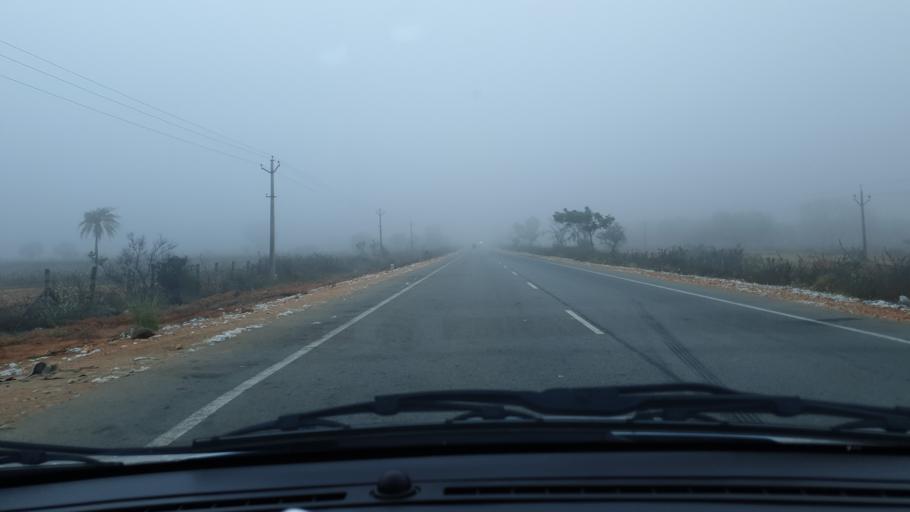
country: IN
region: Telangana
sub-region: Mahbubnagar
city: Nagar Karnul
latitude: 16.6361
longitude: 78.6006
